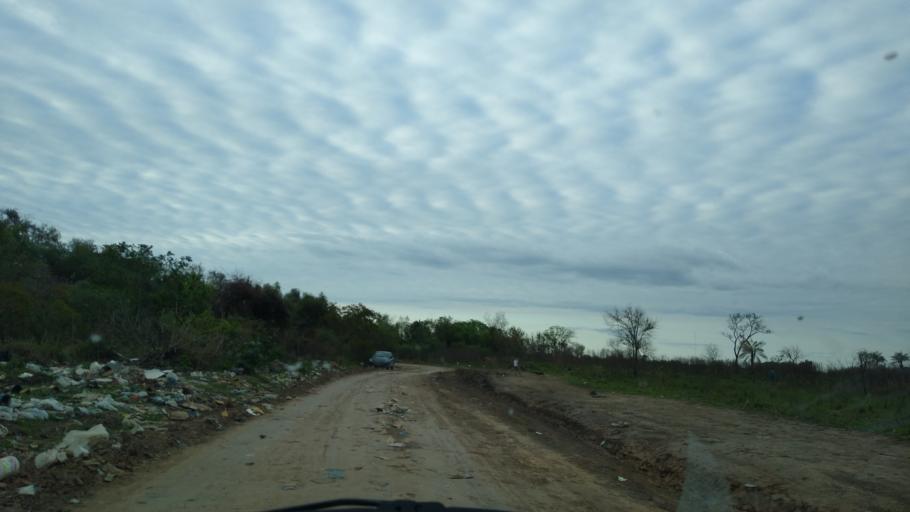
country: AR
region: Chaco
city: Fontana
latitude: -27.3944
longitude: -59.0496
